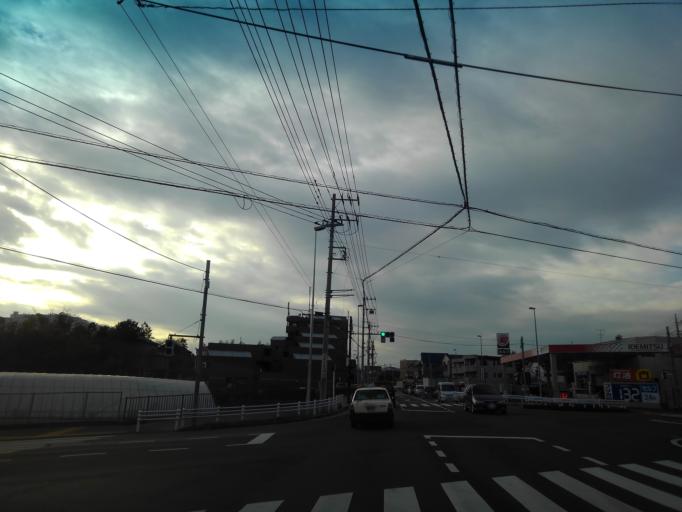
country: JP
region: Tokyo
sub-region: Machida-shi
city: Machida
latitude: 35.5650
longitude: 139.4446
